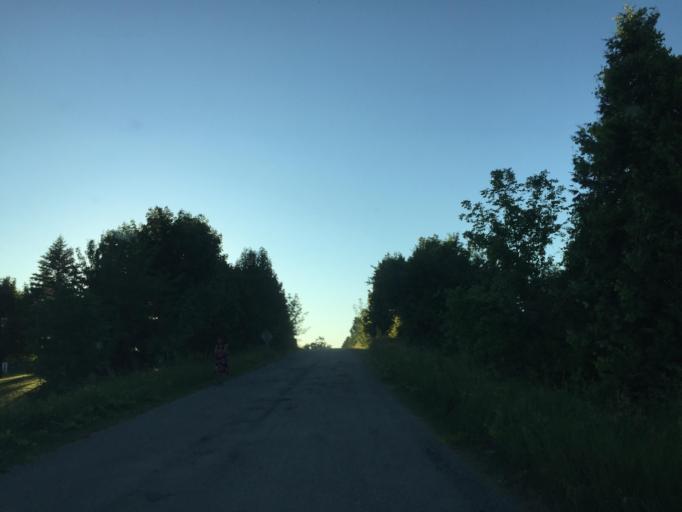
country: CA
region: Ontario
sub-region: Wellington County
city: Guelph
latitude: 43.6006
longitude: -80.2555
